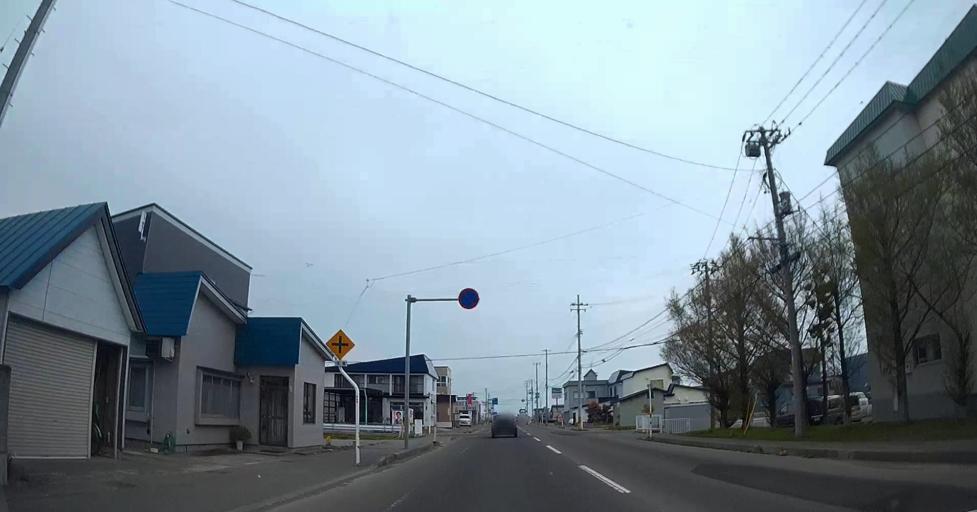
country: JP
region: Aomori
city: Aomori Shi
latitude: 40.8588
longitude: 140.6812
